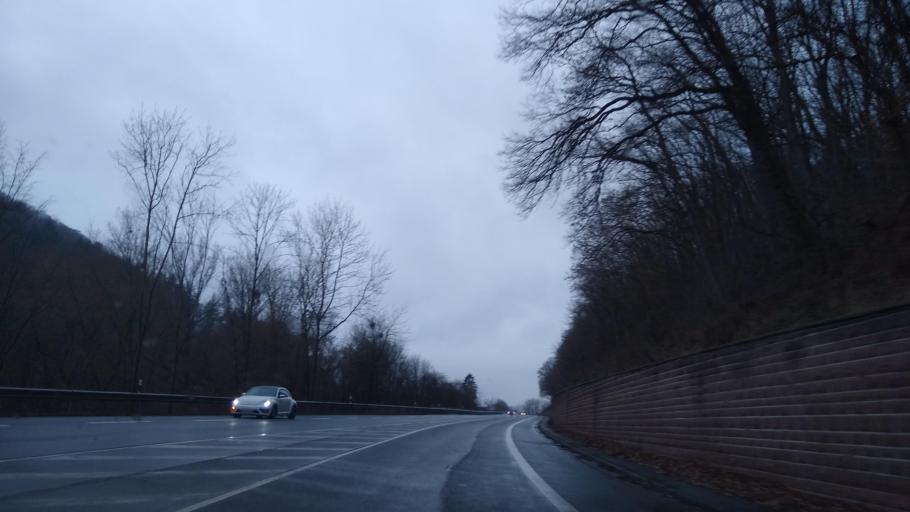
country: DE
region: Lower Saxony
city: Bodenwerder
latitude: 51.9832
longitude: 9.5309
